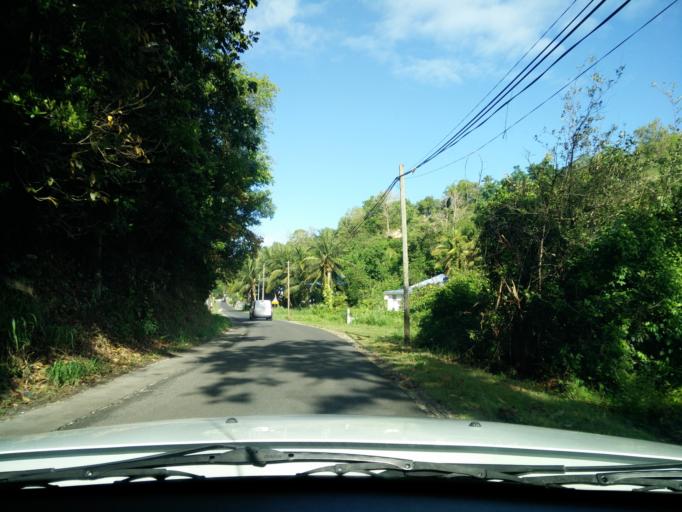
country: GP
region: Guadeloupe
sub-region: Guadeloupe
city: Le Gosier
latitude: 16.2325
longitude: -61.4590
